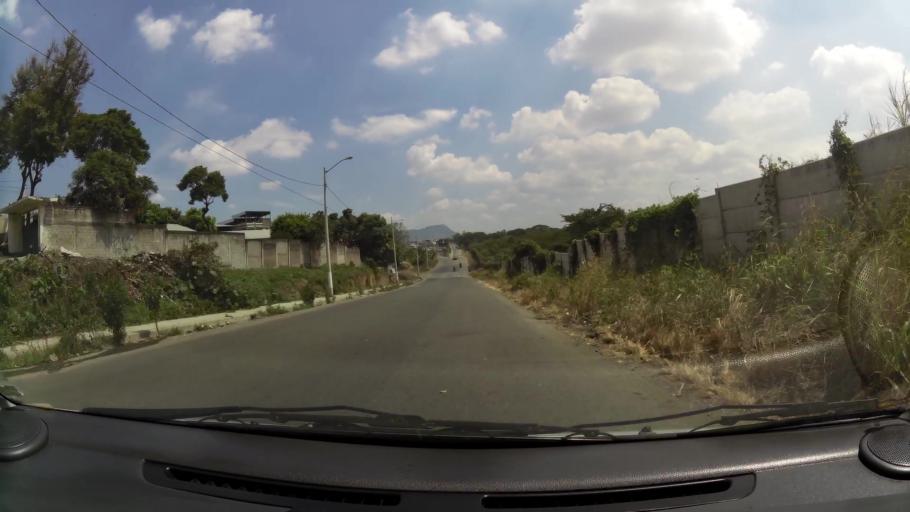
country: EC
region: Guayas
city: Eloy Alfaro
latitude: -2.1149
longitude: -79.9201
